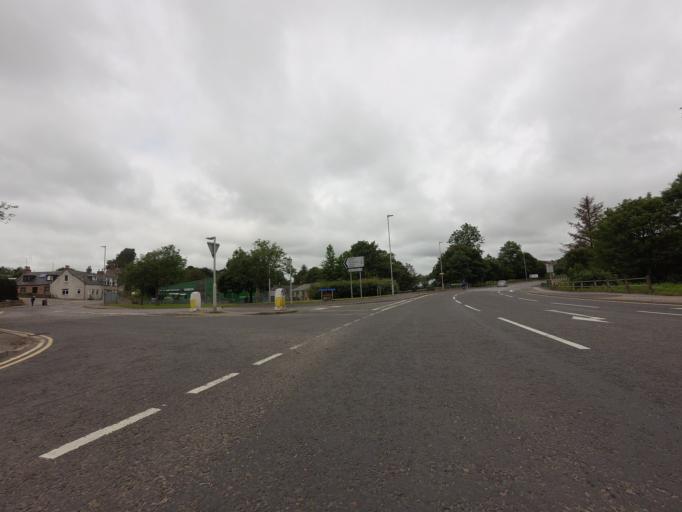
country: GB
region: Scotland
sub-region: Aberdeenshire
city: Turriff
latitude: 57.5333
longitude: -2.4614
